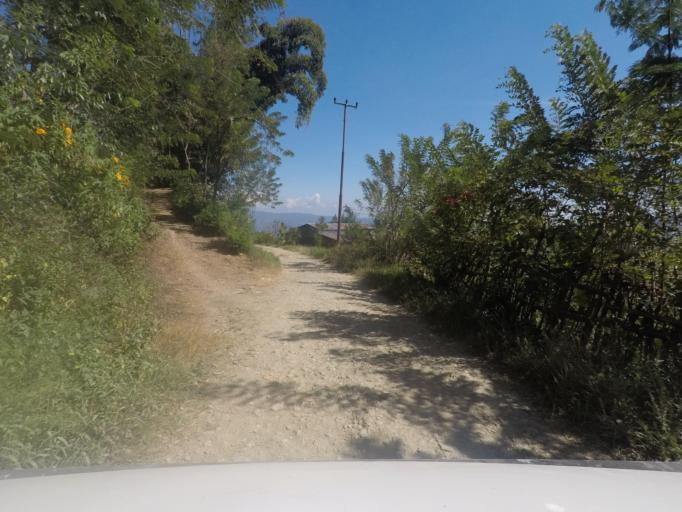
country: TL
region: Ermera
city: Gleno
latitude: -8.7236
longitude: 125.3285
